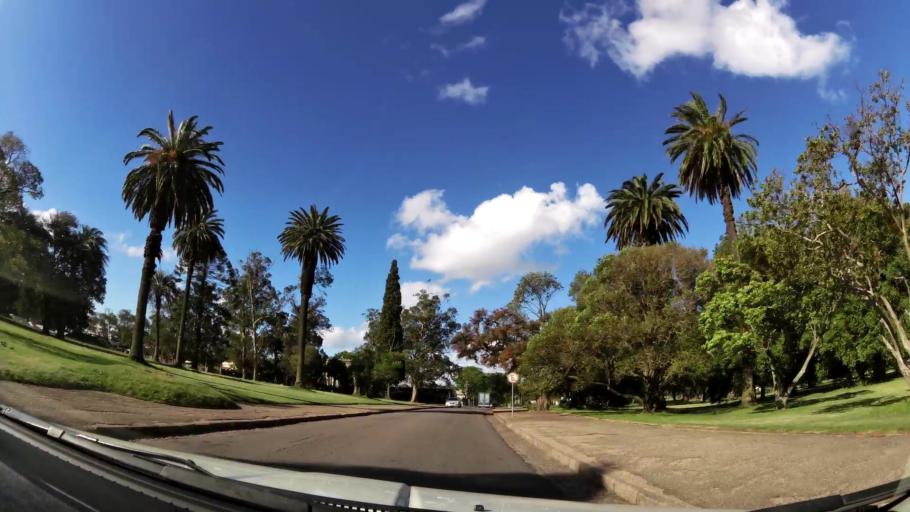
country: UY
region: Montevideo
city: Montevideo
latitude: -34.8568
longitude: -56.2045
